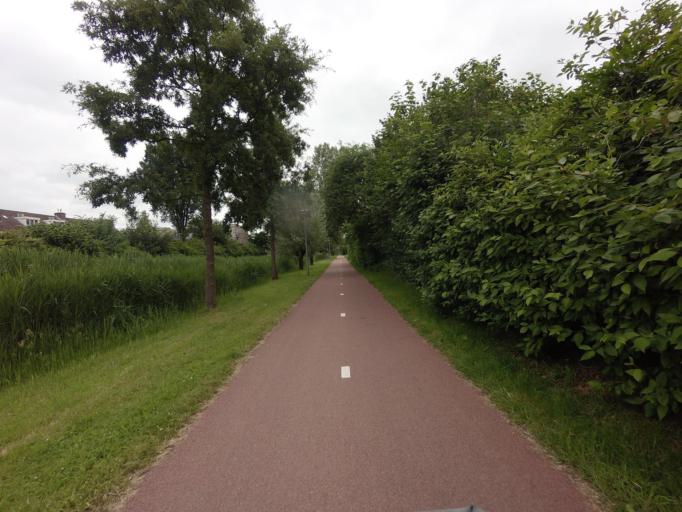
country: NL
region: North Holland
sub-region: Gemeente Huizen
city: Huizen
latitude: 52.2946
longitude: 5.2726
